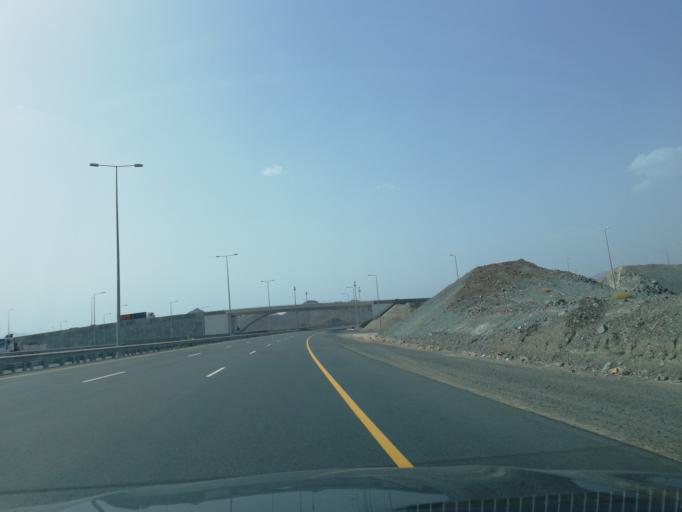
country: OM
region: Ash Sharqiyah
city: Ibra'
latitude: 22.9107
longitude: 58.2652
